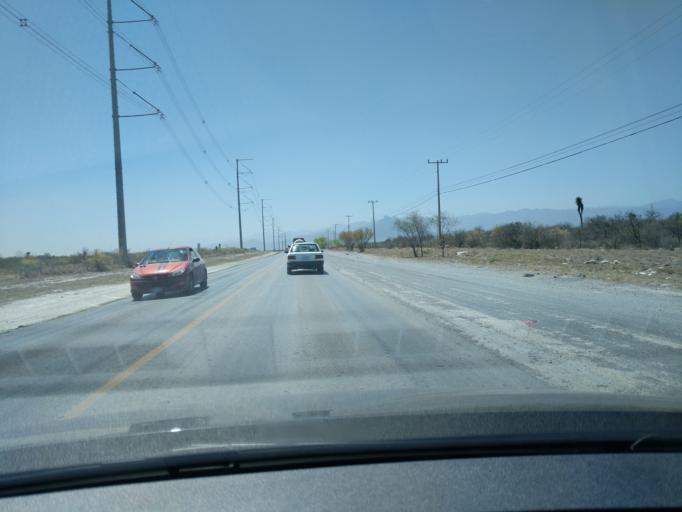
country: MX
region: Nuevo Leon
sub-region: Apodaca
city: Artemio Trevino
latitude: 25.8272
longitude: -100.1431
